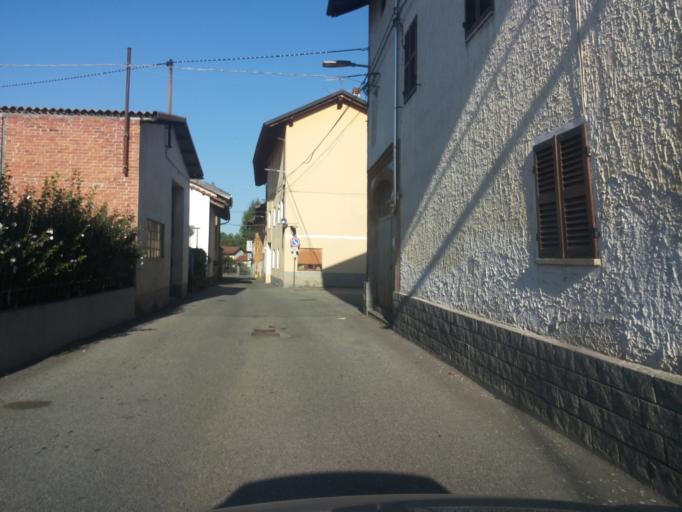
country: IT
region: Piedmont
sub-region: Provincia di Torino
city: Strambino
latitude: 45.3985
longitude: 7.8939
